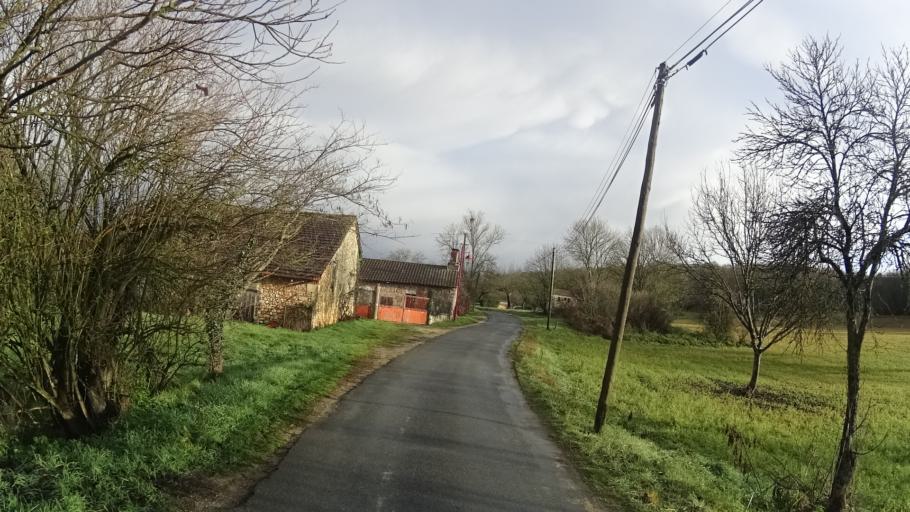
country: FR
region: Aquitaine
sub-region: Departement de la Dordogne
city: Sorges
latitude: 45.2464
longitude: 0.8982
